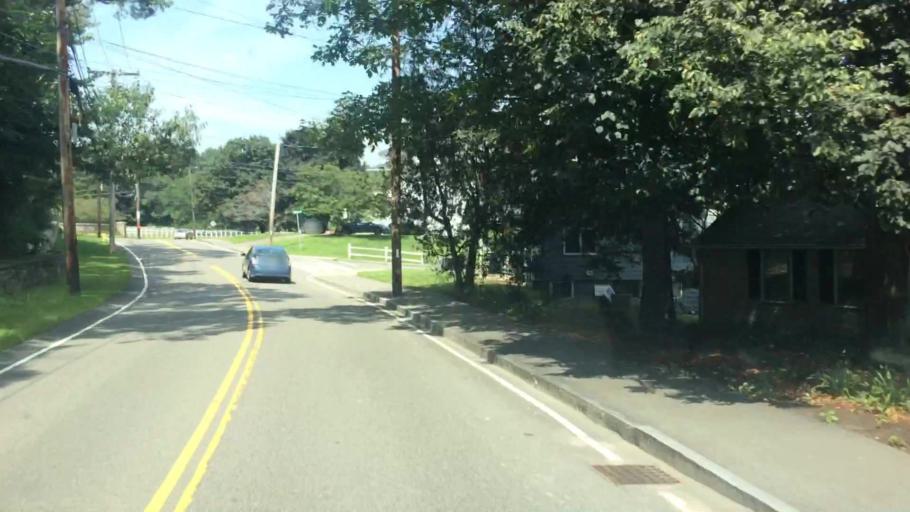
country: US
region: Massachusetts
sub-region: Norfolk County
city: Dedham
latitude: 42.2626
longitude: -71.1821
